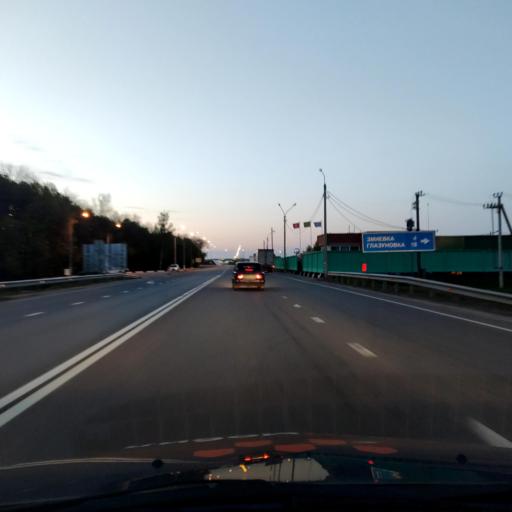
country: RU
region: Orjol
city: Zmiyevka
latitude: 52.7046
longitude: 36.3666
